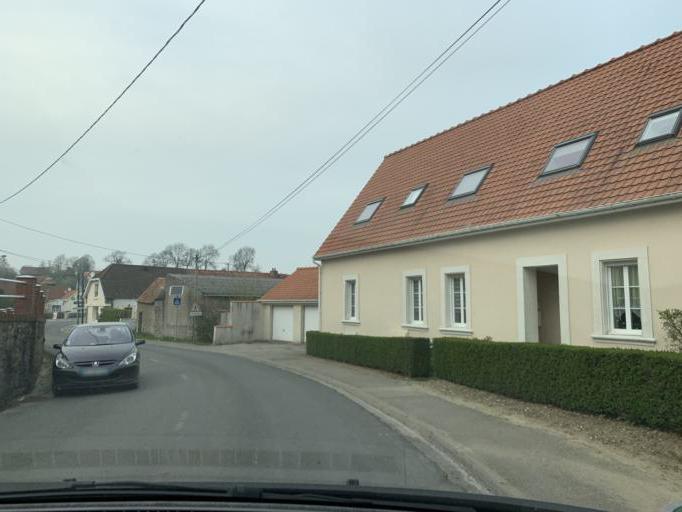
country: FR
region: Nord-Pas-de-Calais
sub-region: Departement du Pas-de-Calais
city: Samer
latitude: 50.6836
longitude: 1.7609
